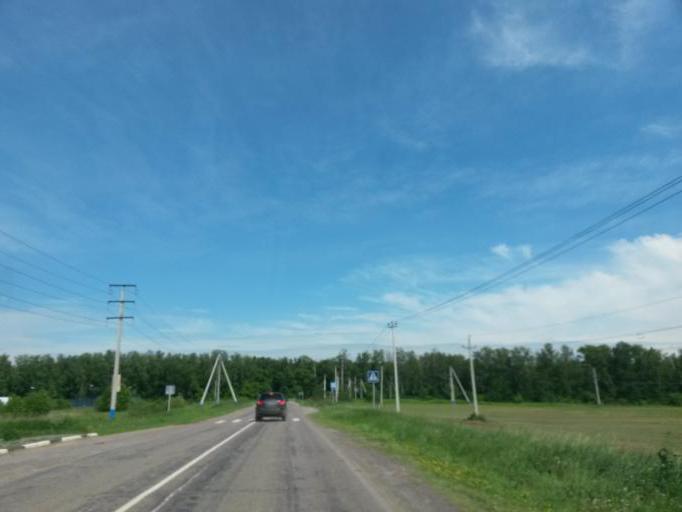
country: RU
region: Moskovskaya
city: Barybino
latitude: 55.2266
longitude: 37.8635
